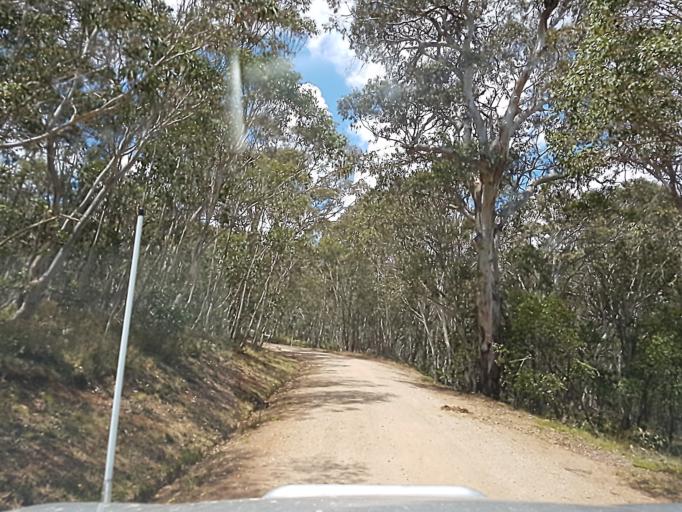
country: AU
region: New South Wales
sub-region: Snowy River
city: Jindabyne
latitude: -36.8974
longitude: 148.0918
